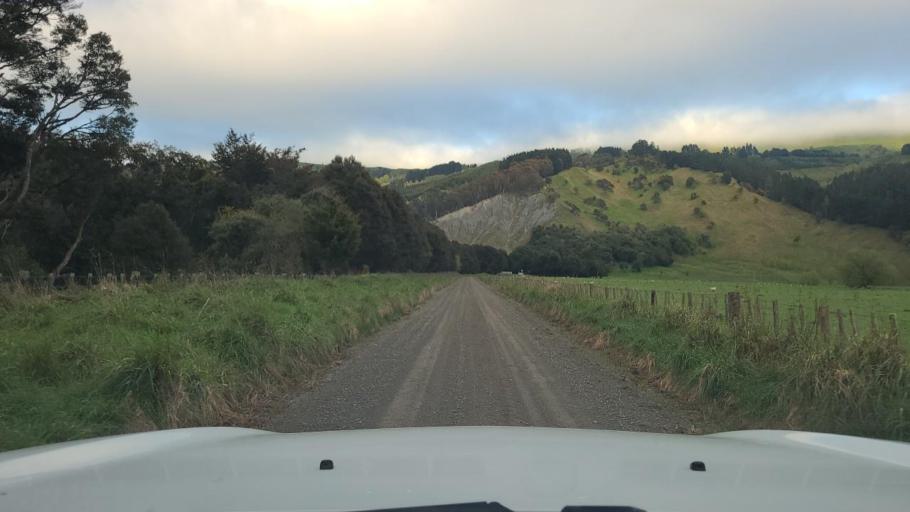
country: NZ
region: Wellington
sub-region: Masterton District
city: Masterton
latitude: -41.1782
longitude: 175.6911
